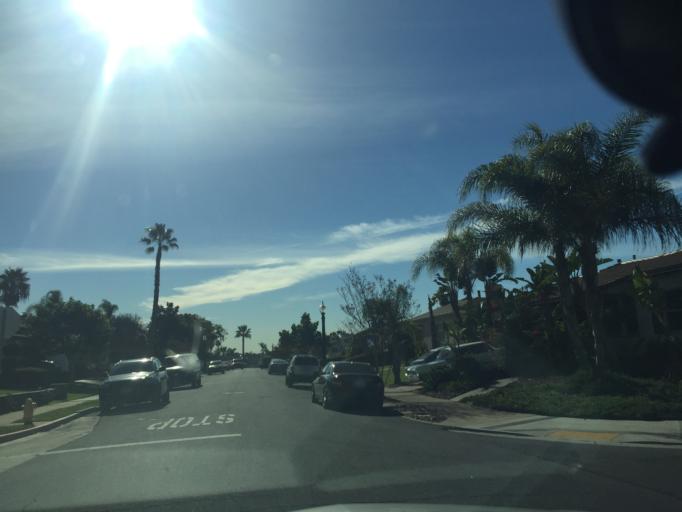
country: US
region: California
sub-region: San Diego County
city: Lemon Grove
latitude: 32.7611
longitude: -117.0907
